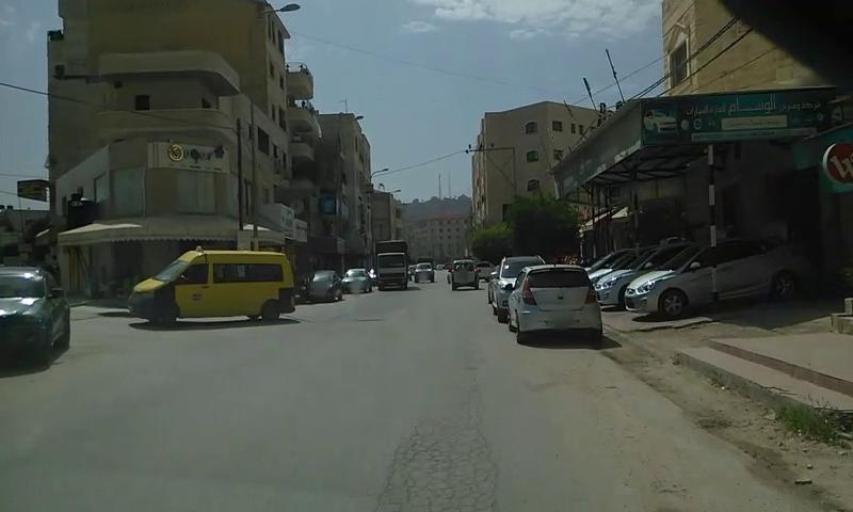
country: PS
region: West Bank
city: Janin
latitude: 32.4666
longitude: 35.2928
